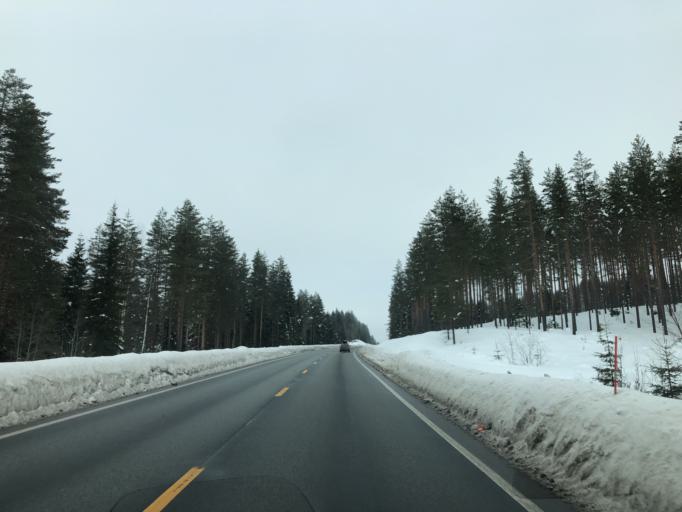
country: NO
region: Hedmark
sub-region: Elverum
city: Elverum
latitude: 60.9562
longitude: 11.7044
